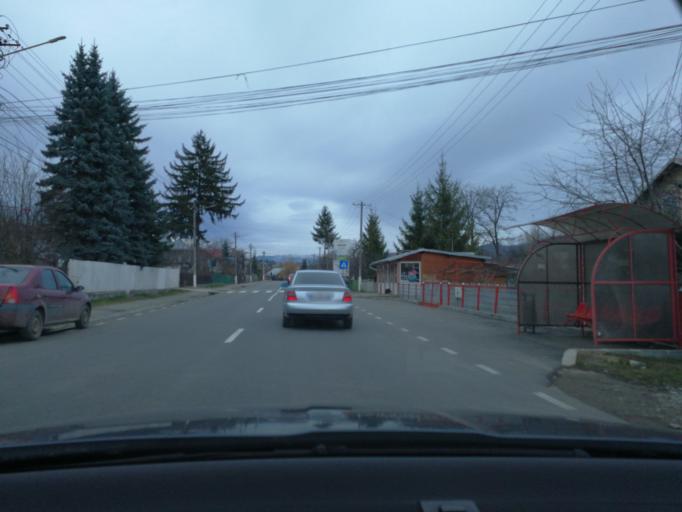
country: RO
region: Prahova
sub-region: Comuna Poiana Campina
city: Poiana Campina
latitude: 45.1446
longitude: 25.6933
